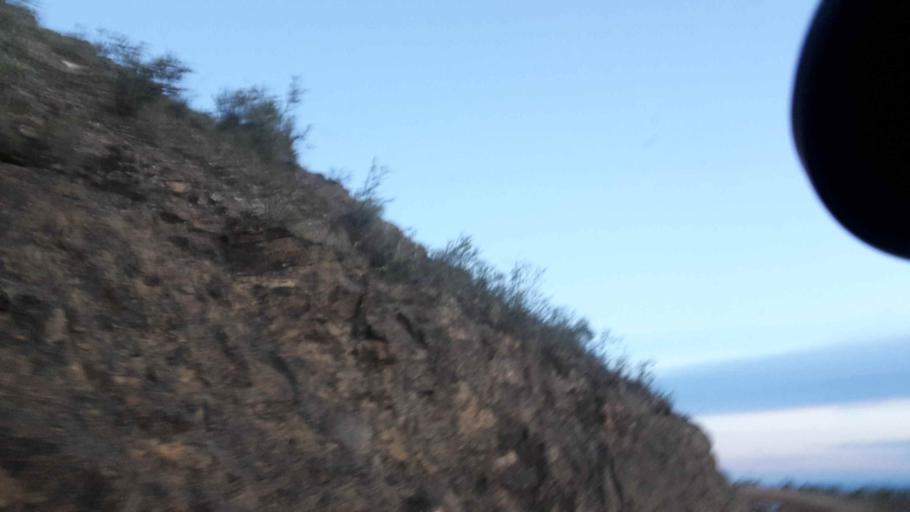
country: BO
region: Cochabamba
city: Mizque
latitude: -17.9222
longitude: -65.5003
